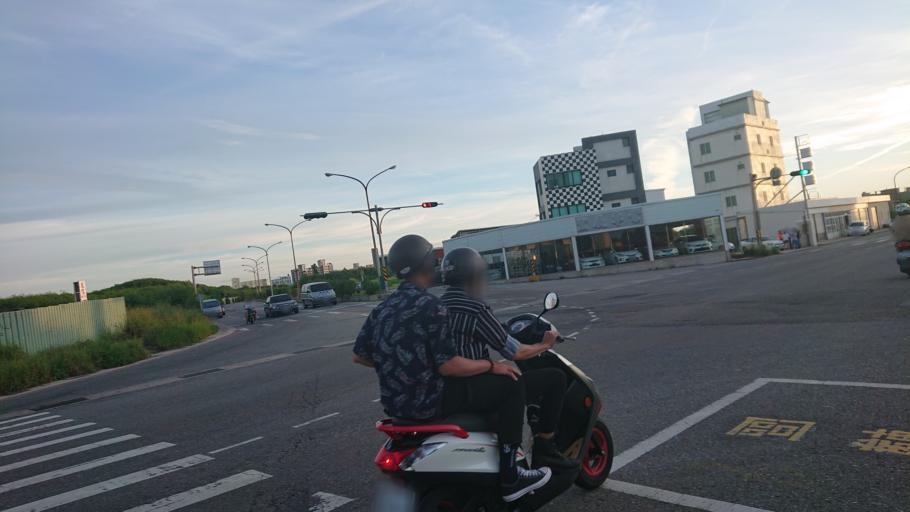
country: TW
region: Taiwan
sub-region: Penghu
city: Ma-kung
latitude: 23.5692
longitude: 119.5899
